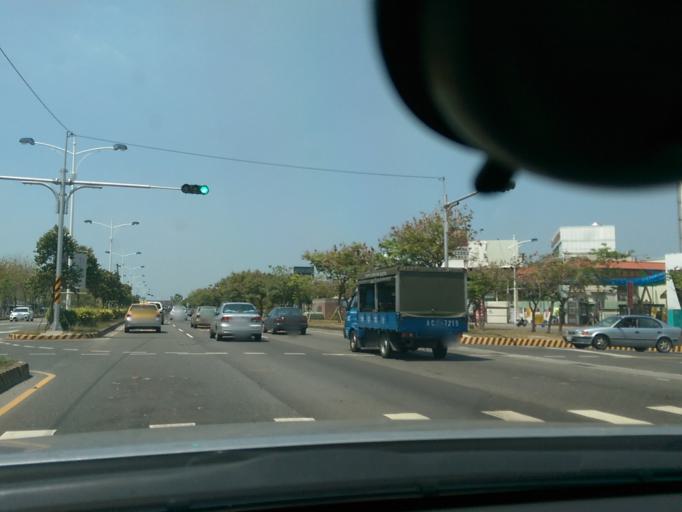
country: TW
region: Taiwan
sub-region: Chiayi
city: Jiayi Shi
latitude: 23.5022
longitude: 120.4490
